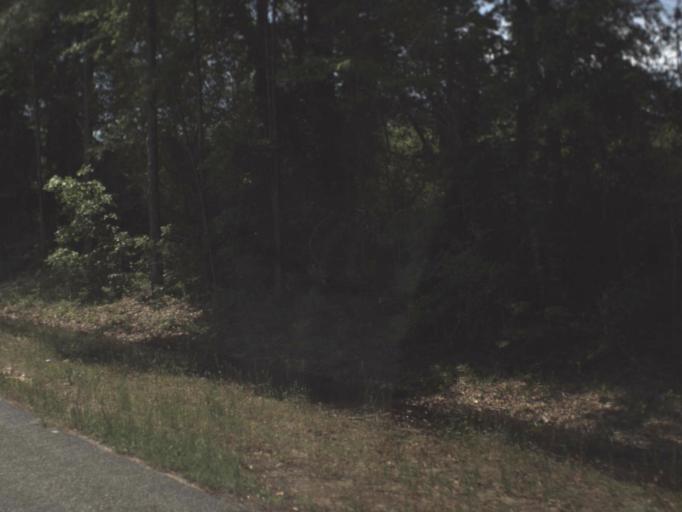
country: US
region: Florida
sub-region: Jackson County
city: Marianna
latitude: 30.6344
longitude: -85.1891
